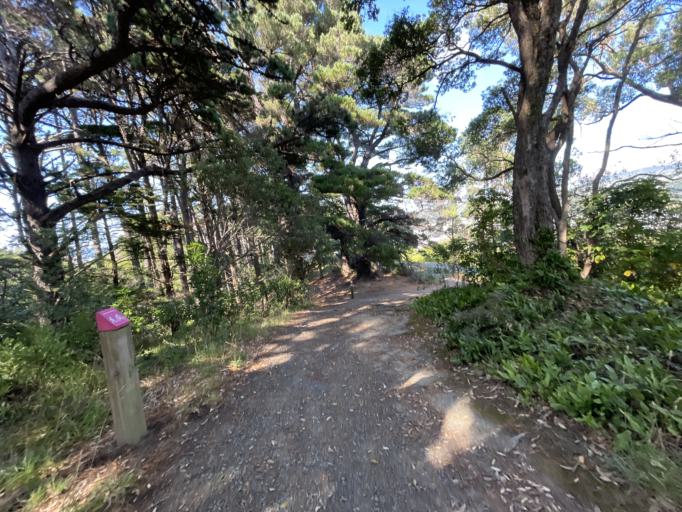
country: NZ
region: Wellington
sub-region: Wellington City
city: Wellington
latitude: -41.3077
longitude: 174.7883
